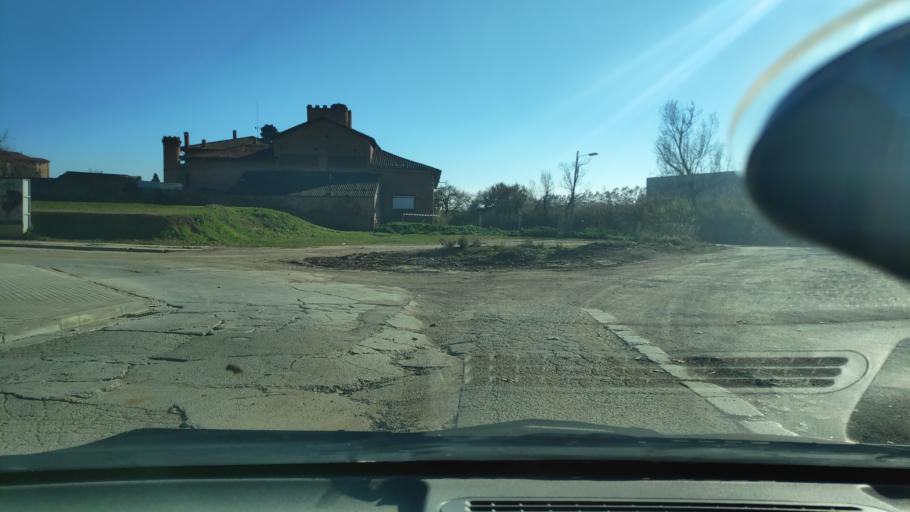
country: ES
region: Catalonia
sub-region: Provincia de Barcelona
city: Sant Quirze del Valles
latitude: 41.5402
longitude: 2.0927
